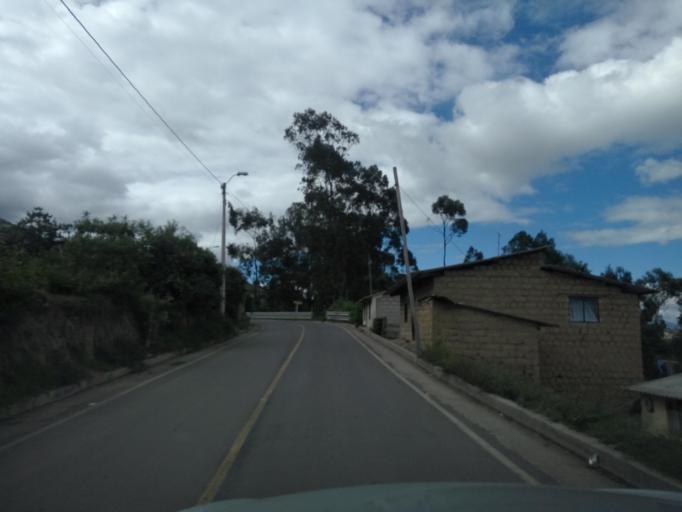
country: EC
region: Imbabura
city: Atuntaqui
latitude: 0.4062
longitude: -78.2475
